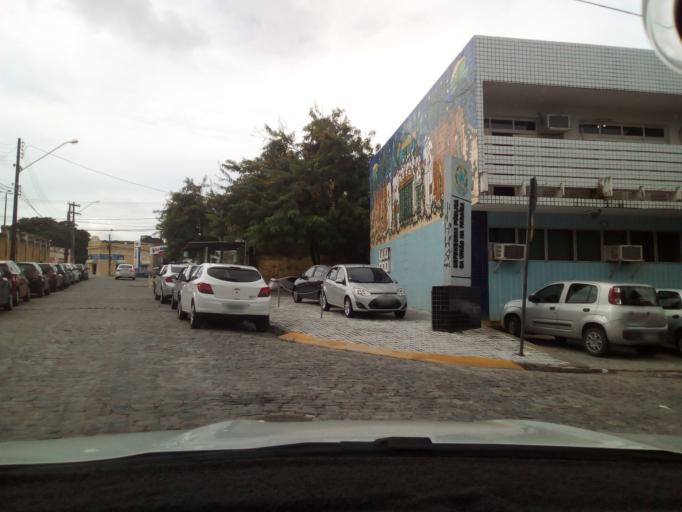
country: BR
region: Paraiba
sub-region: Joao Pessoa
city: Joao Pessoa
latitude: -7.1167
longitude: -34.8818
